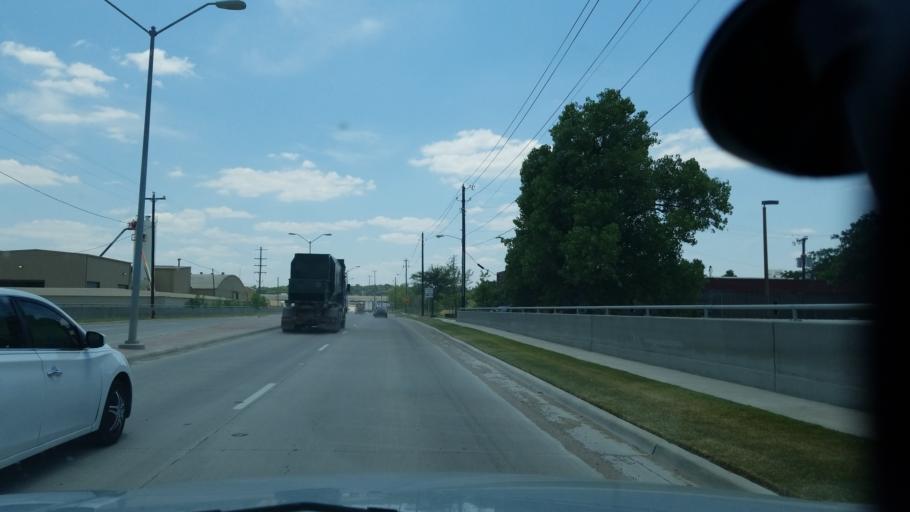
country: US
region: Texas
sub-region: Dallas County
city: Grand Prairie
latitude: 32.7657
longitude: -96.9603
